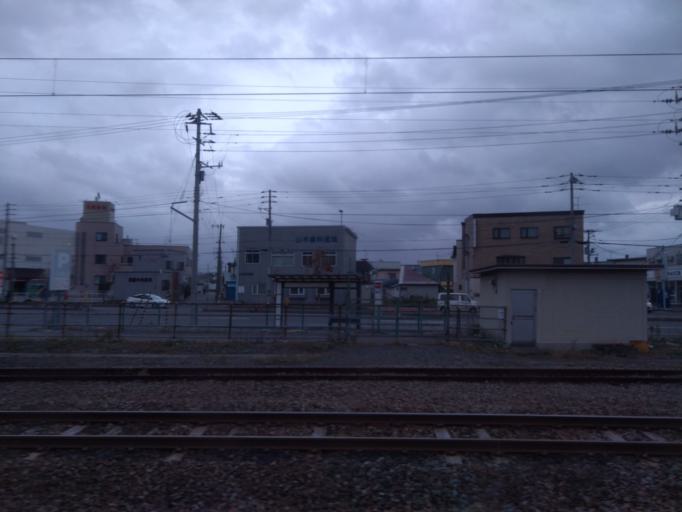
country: JP
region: Hokkaido
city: Hakodate
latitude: 41.8020
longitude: 140.7340
